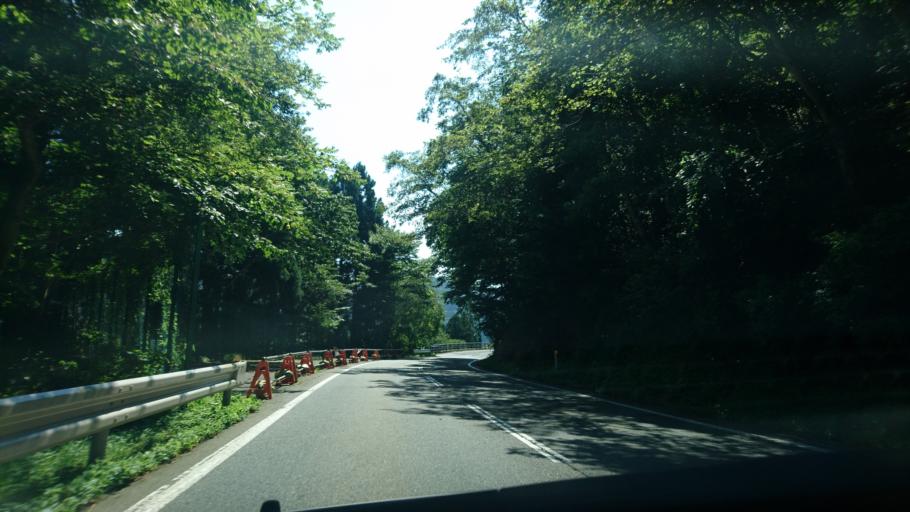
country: JP
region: Iwate
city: Ofunato
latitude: 39.0141
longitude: 141.4447
